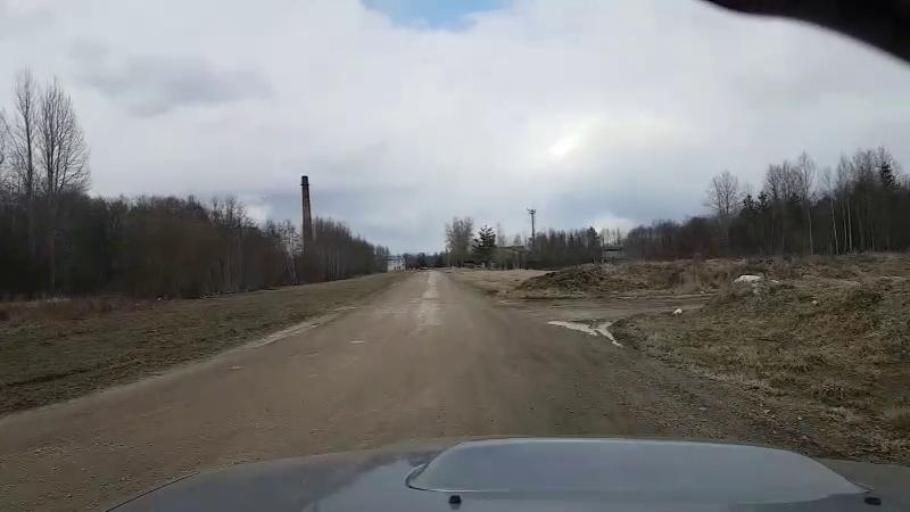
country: EE
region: Jaervamaa
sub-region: Paide linn
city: Paide
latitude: 58.8779
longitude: 25.5512
